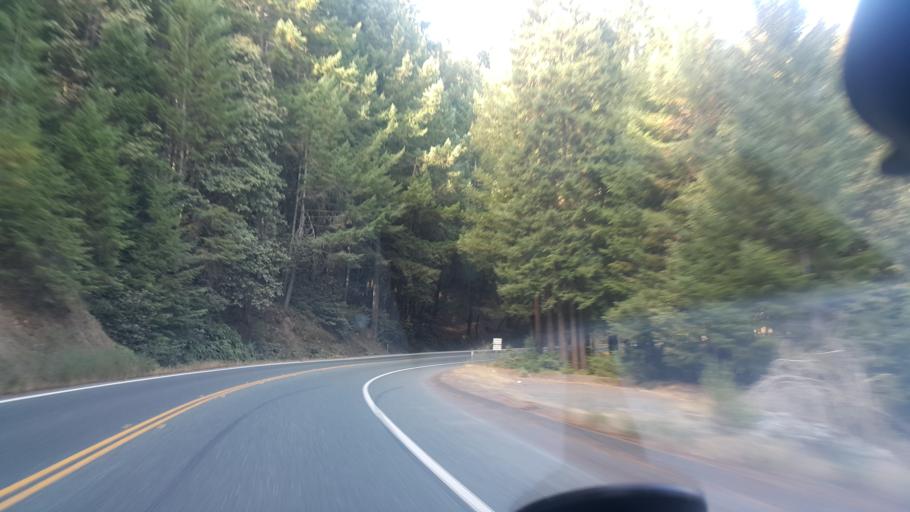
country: US
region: California
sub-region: Mendocino County
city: Brooktrails
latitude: 39.3929
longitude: -123.4610
